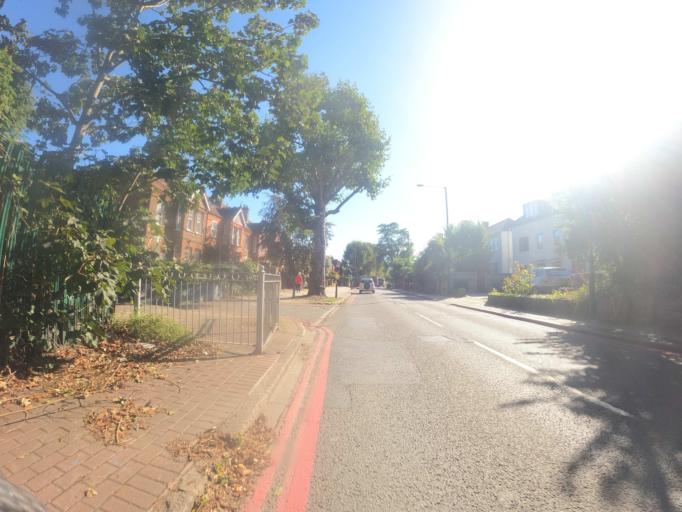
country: GB
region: England
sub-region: Greater London
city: Brentford
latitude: 51.4804
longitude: -0.2830
